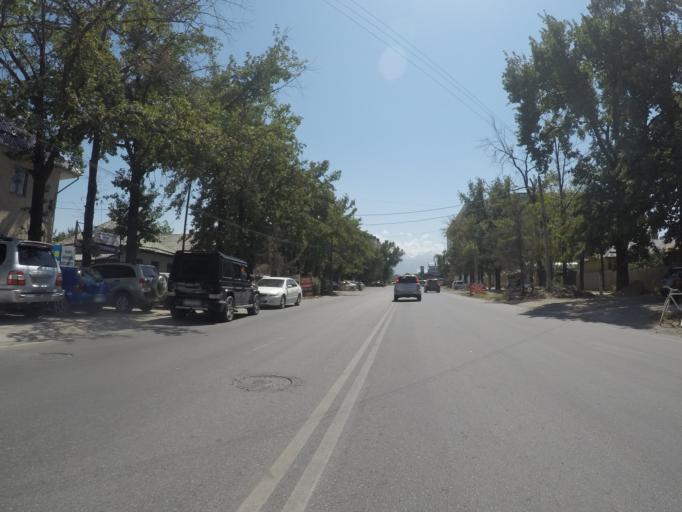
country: KG
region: Chuy
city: Bishkek
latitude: 42.8447
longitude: 74.5769
